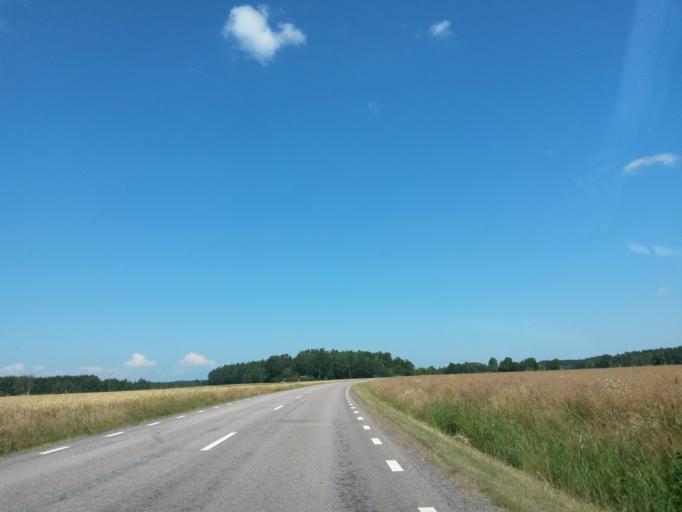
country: SE
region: Vaestra Goetaland
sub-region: Grastorps Kommun
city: Graestorp
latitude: 58.3096
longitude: 12.6693
